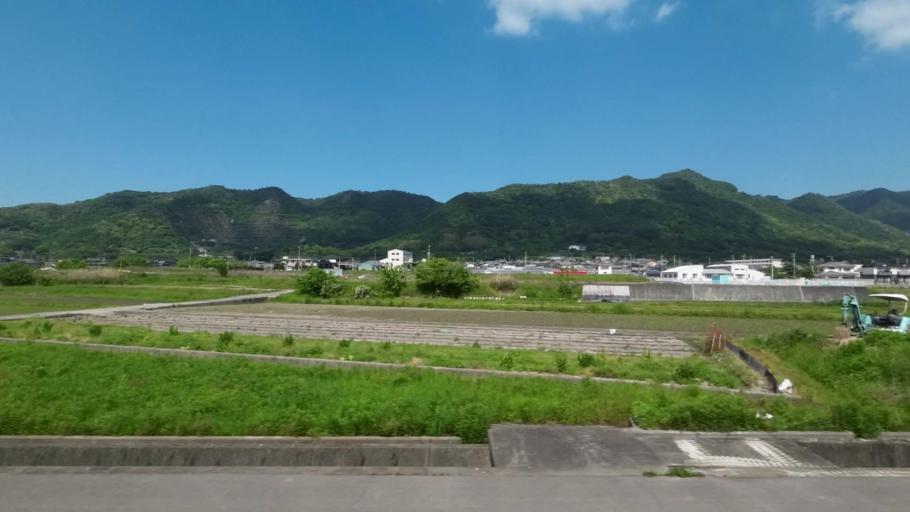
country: JP
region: Kagawa
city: Kan'onjicho
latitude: 34.1504
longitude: 133.6871
